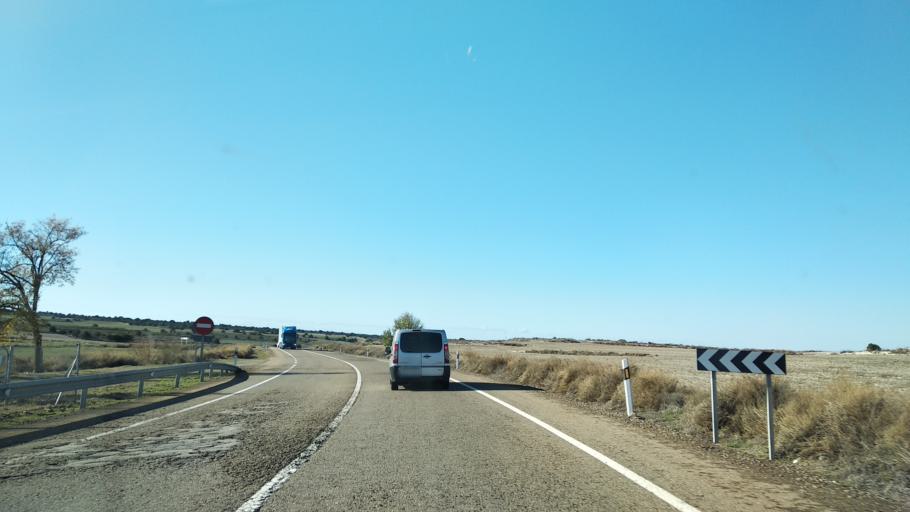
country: ES
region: Aragon
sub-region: Provincia de Zaragoza
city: Bujaraloz
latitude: 41.4950
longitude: -0.2251
